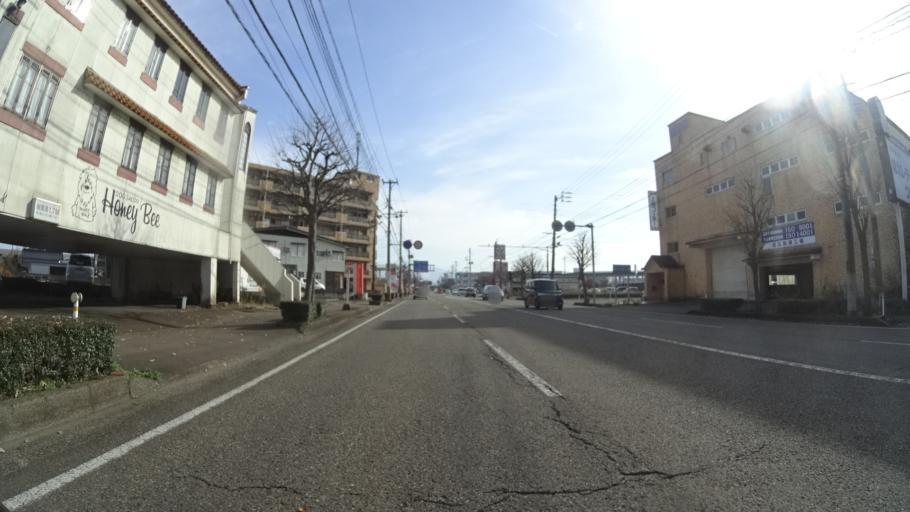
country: JP
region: Niigata
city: Joetsu
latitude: 37.1263
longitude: 138.2489
